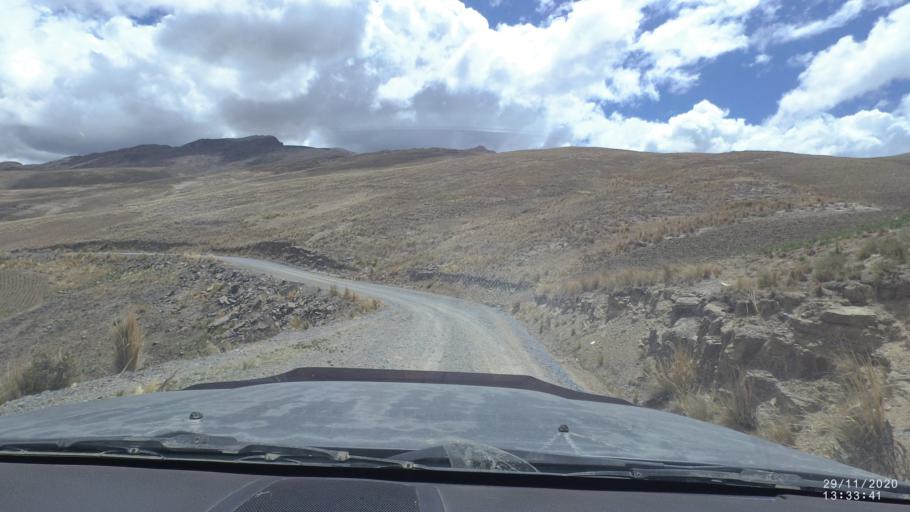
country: BO
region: Cochabamba
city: Cochabamba
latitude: -17.1073
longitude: -66.3367
